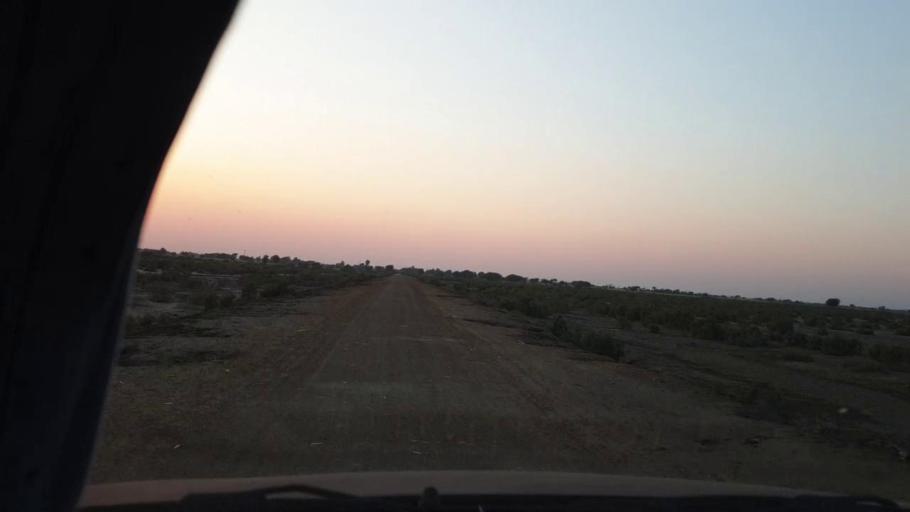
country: PK
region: Sindh
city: Jhol
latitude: 25.9365
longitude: 68.9666
